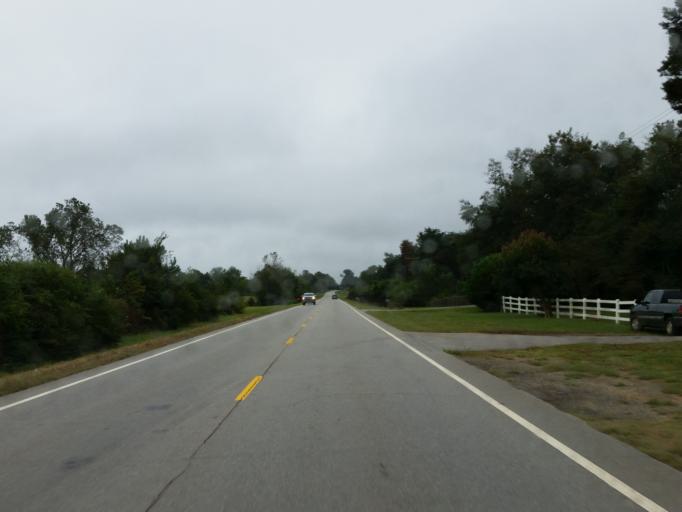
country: US
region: Georgia
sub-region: Lamar County
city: Barnesville
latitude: 32.9763
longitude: -84.1149
